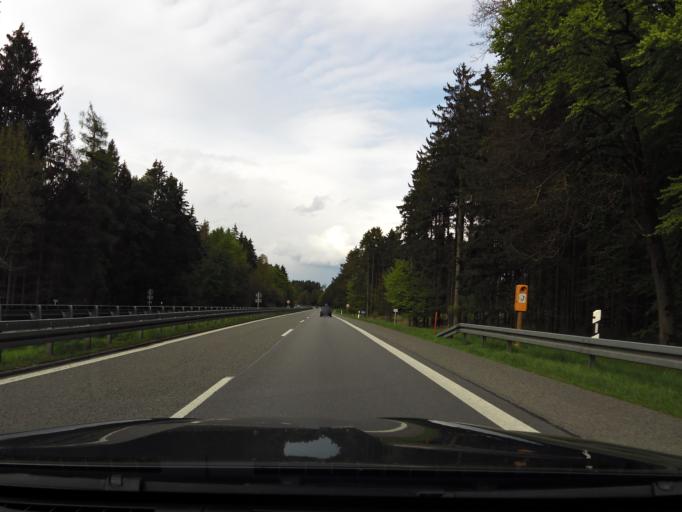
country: DE
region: Bavaria
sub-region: Upper Bavaria
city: Wolnzach
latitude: 48.6161
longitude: 11.6947
